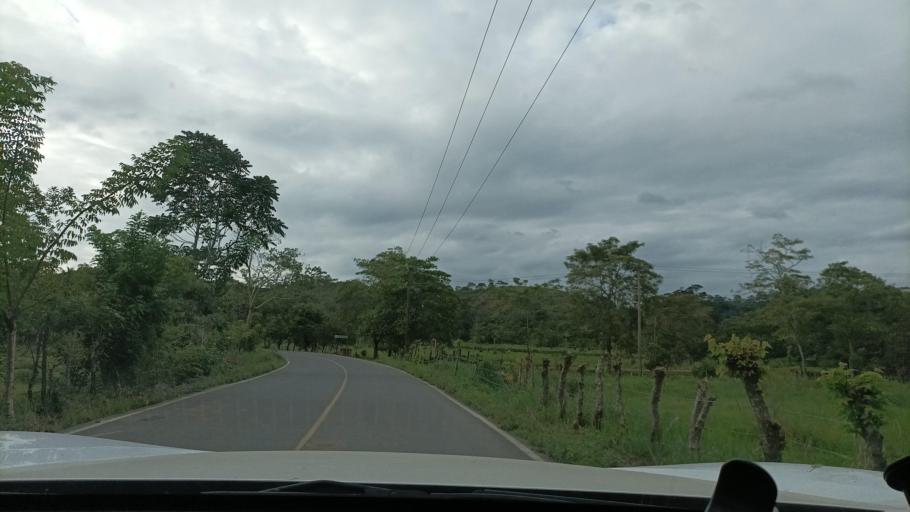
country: MX
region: Veracruz
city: Hidalgotitlan
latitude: 17.7206
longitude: -94.4817
